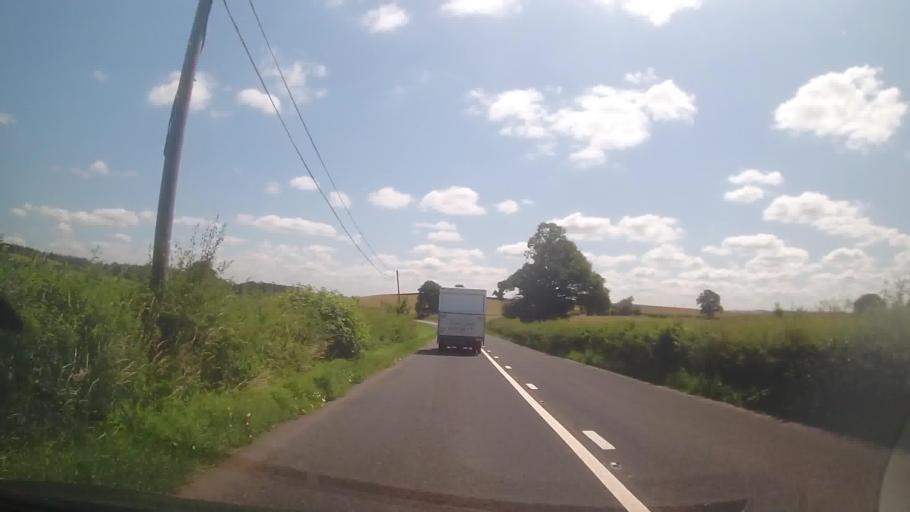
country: GB
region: England
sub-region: Herefordshire
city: Ocle Pychard
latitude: 52.1363
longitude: -2.6111
